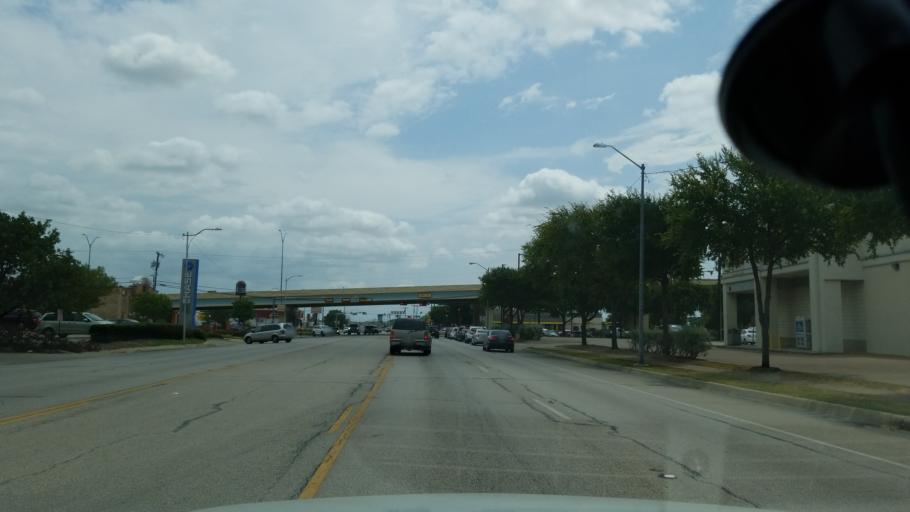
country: US
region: Texas
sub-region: Dallas County
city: Grand Prairie
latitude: 32.7459
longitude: -96.9960
